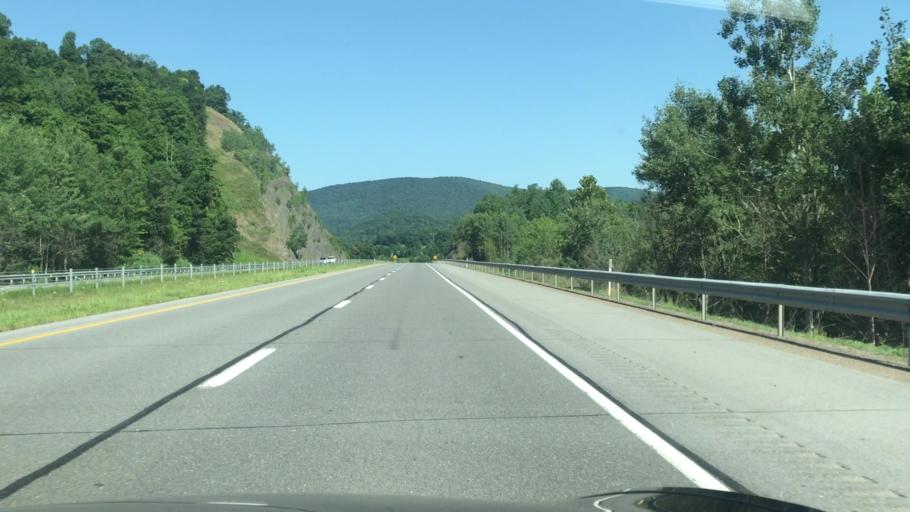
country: US
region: Pennsylvania
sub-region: Lycoming County
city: Garden View
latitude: 41.3146
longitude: -77.0891
